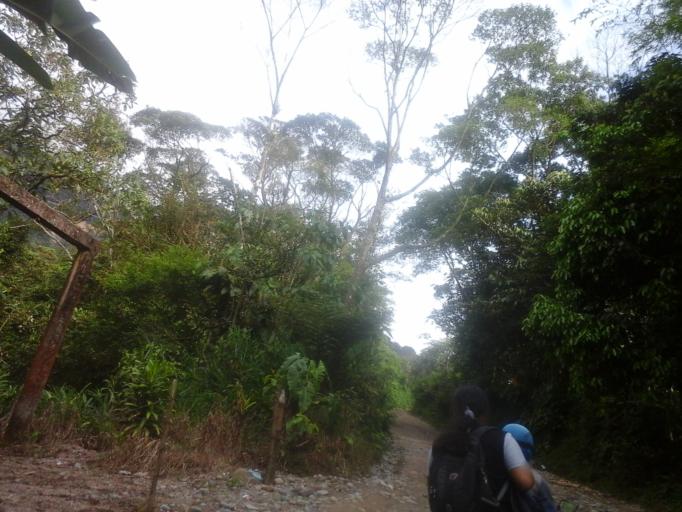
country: CO
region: Putumayo
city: Mocoa
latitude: 1.1828
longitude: -76.6751
